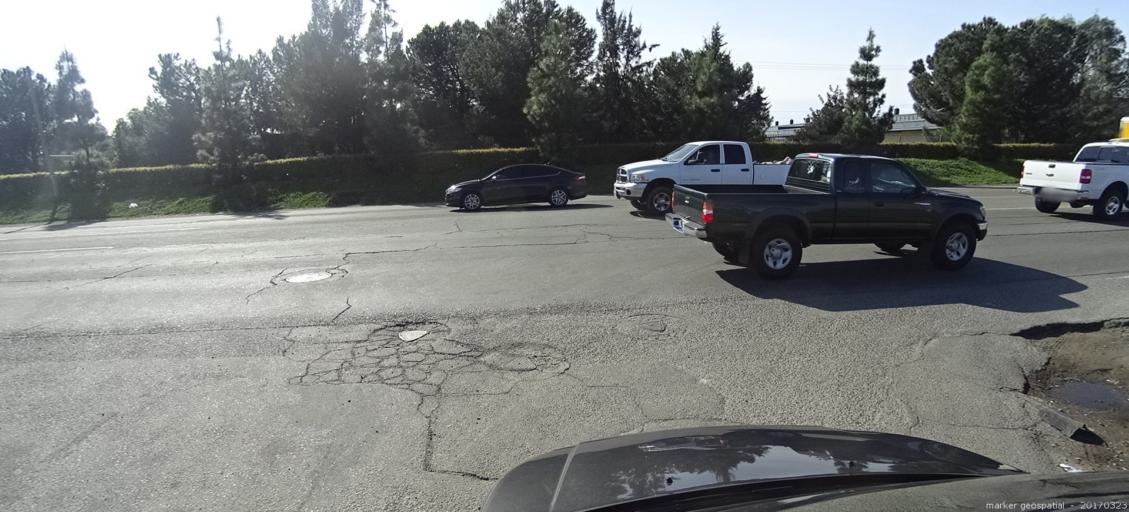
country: US
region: California
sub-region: Sacramento County
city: Florin
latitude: 38.5215
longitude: -121.3905
